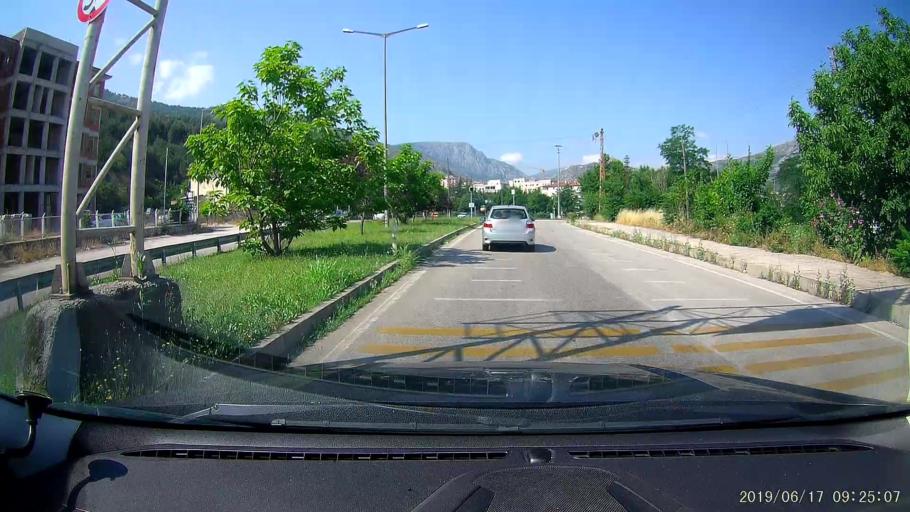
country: TR
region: Amasya
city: Amasya
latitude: 40.6683
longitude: 35.8517
